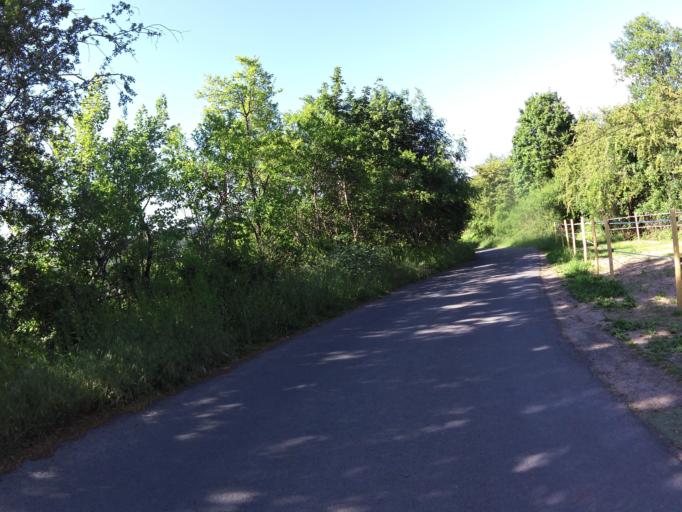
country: DE
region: Hesse
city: Philippsthal
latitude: 50.8347
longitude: 9.9942
